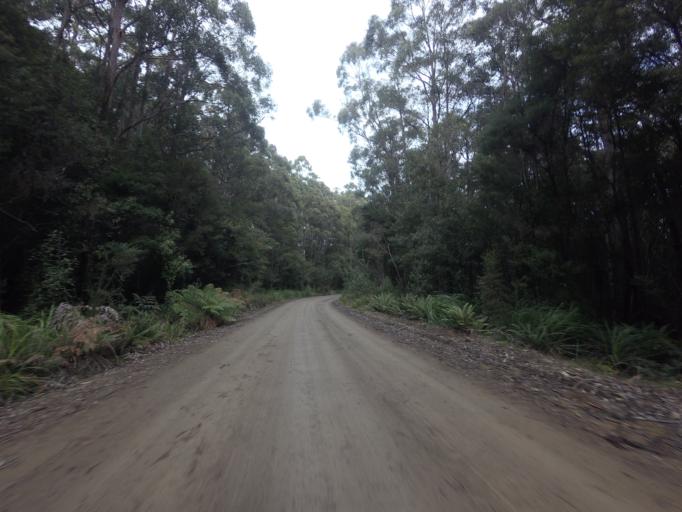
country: AU
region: Tasmania
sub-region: Huon Valley
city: Geeveston
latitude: -43.4930
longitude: 146.8870
